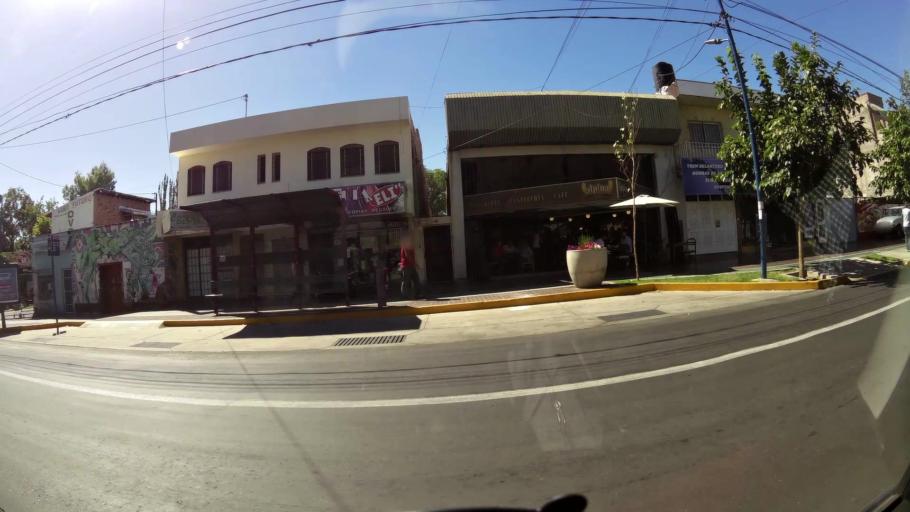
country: AR
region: Mendoza
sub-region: Departamento de Godoy Cruz
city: Godoy Cruz
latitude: -32.9069
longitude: -68.8605
